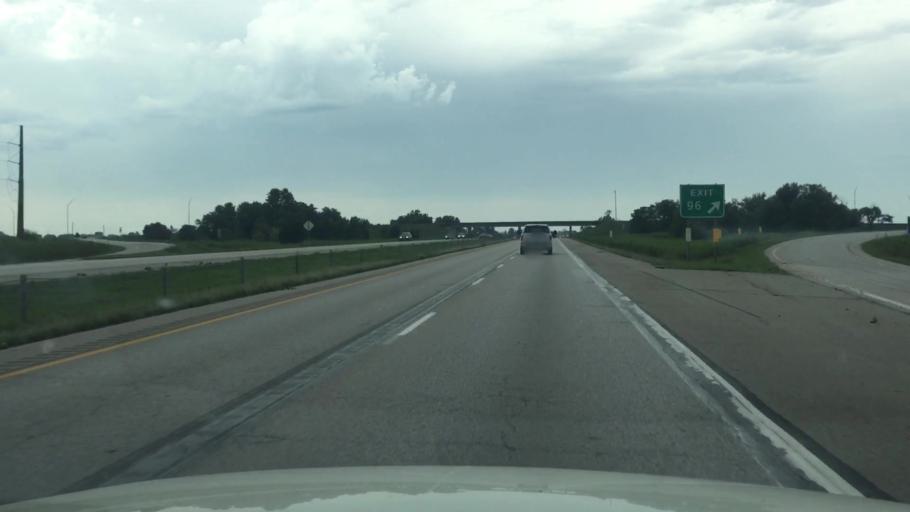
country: US
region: Iowa
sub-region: Polk County
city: Ankeny
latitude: 41.7947
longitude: -93.5706
